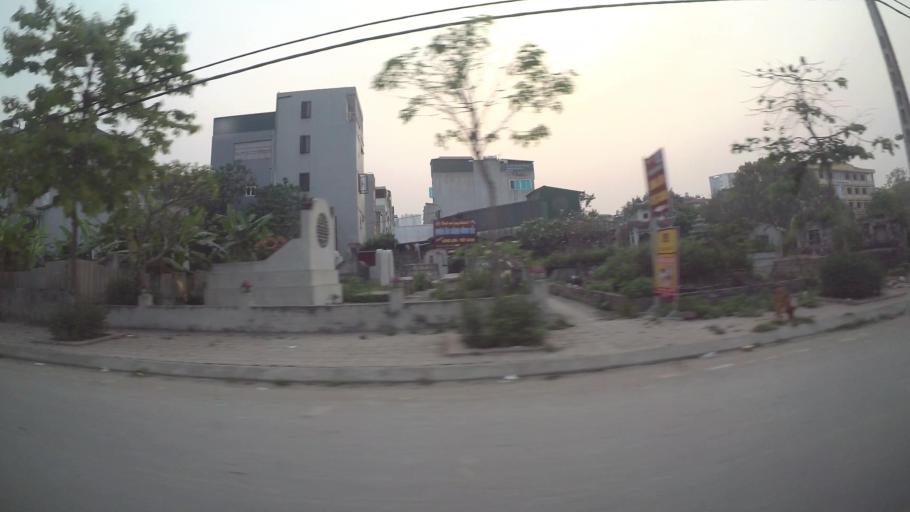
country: VN
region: Ha Noi
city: Thanh Xuan
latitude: 20.9783
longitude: 105.7990
